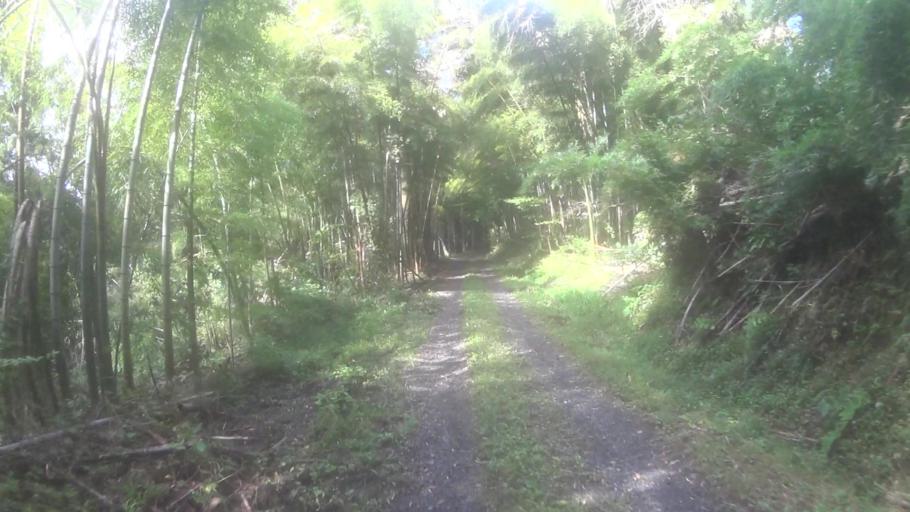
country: JP
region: Kyoto
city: Miyazu
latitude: 35.6249
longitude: 135.1623
